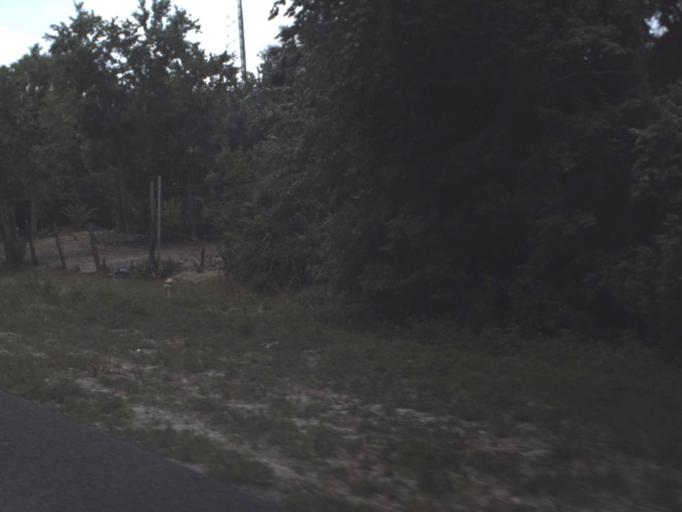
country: US
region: Florida
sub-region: Brevard County
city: Titusville
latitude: 28.5498
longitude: -80.8364
